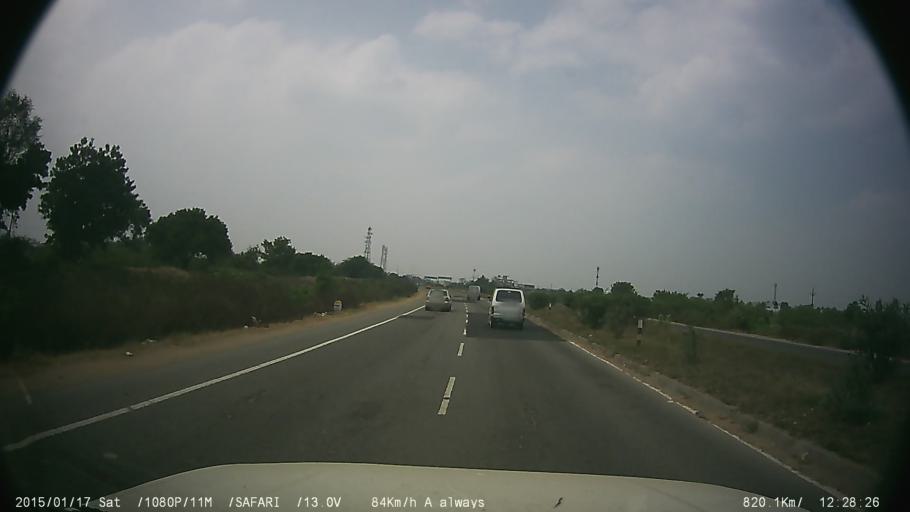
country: IN
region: Tamil Nadu
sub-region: Kancheepuram
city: Kanchipuram
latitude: 12.8721
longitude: 79.7031
